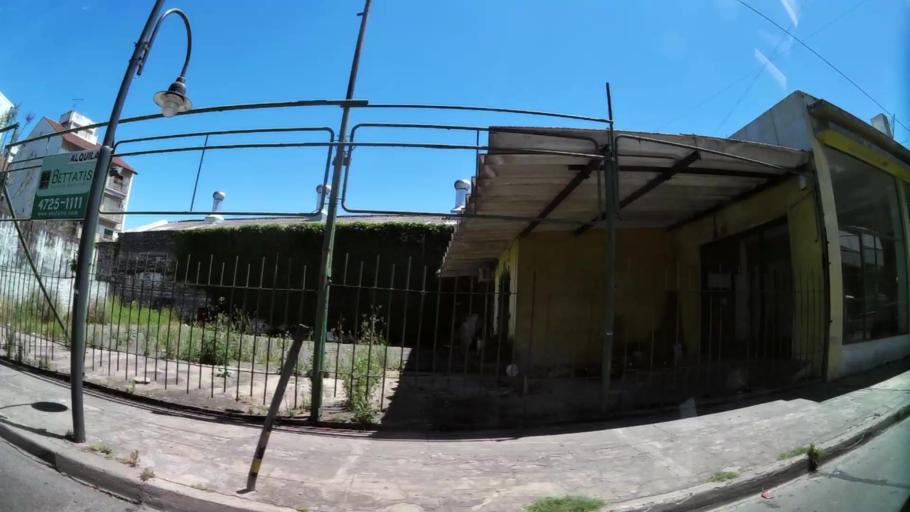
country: AR
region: Buenos Aires
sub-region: Partido de Tigre
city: Tigre
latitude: -34.4475
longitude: -58.5472
